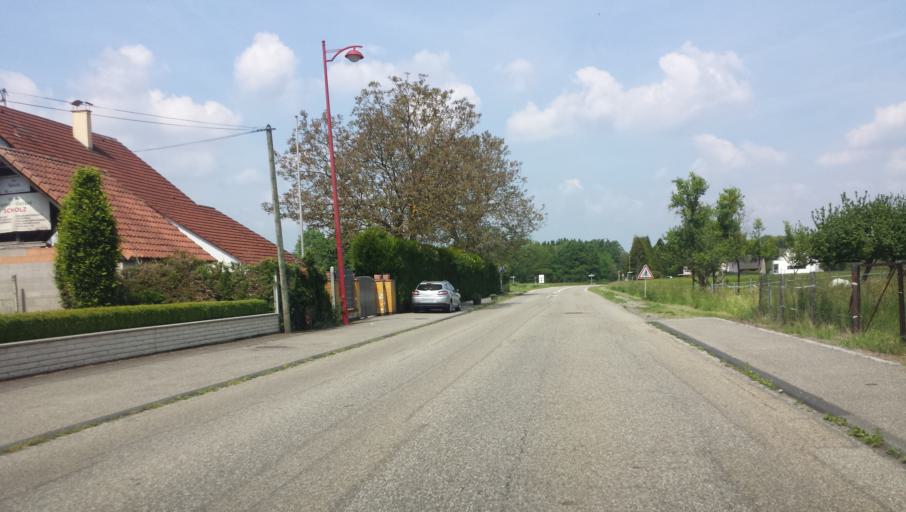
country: DE
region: Rheinland-Pfalz
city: Scheibenhardt
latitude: 48.9772
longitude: 8.1335
